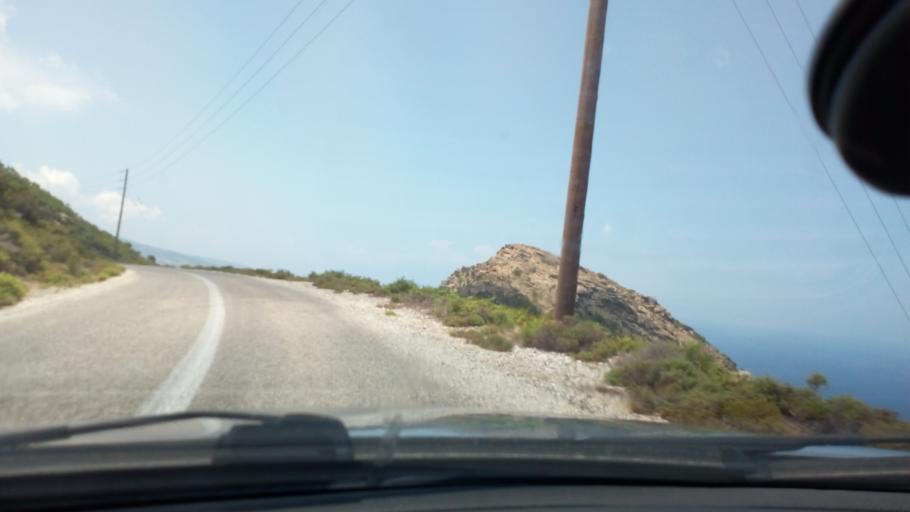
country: GR
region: North Aegean
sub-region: Nomos Samou
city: Agios Kirykos
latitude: 37.6402
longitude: 26.2534
